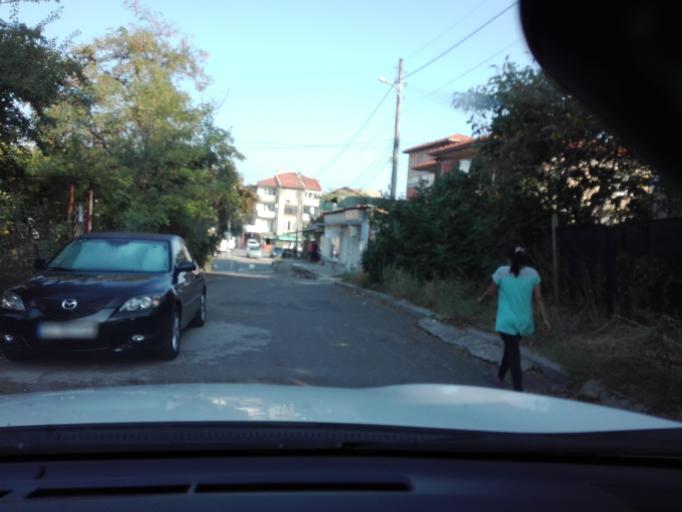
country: BG
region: Burgas
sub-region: Obshtina Burgas
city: Burgas
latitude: 42.4603
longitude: 27.4092
